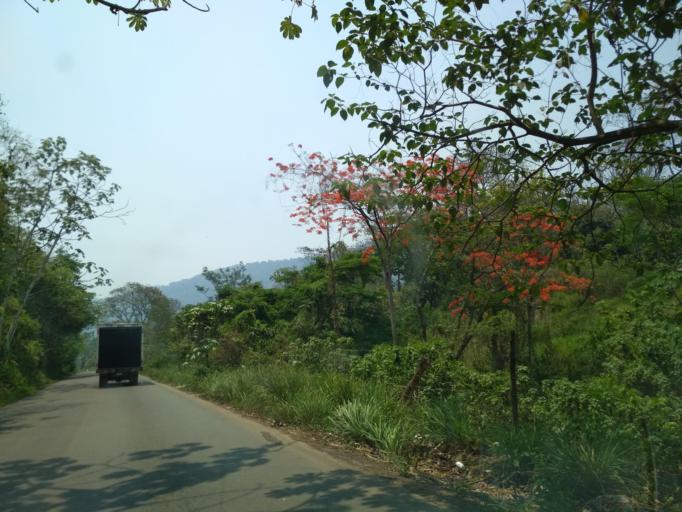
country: MX
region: Veracruz
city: Tezonapa
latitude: 18.6065
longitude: -96.6914
